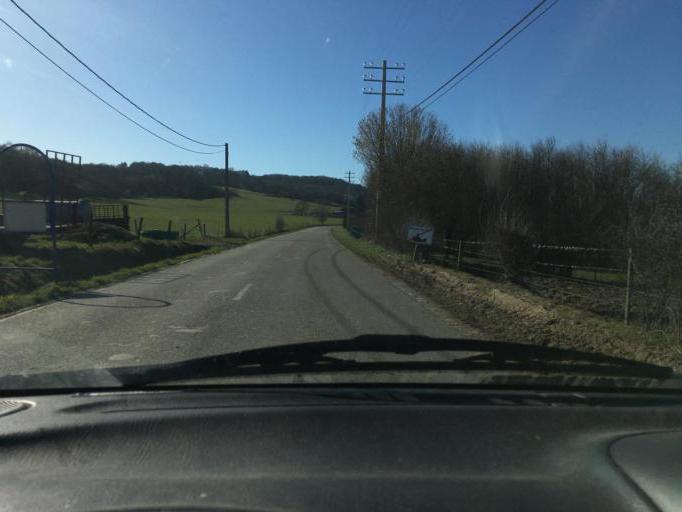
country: FR
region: Champagne-Ardenne
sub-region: Departement des Ardennes
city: Vireux-Molhain
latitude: 50.1173
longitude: 4.6407
